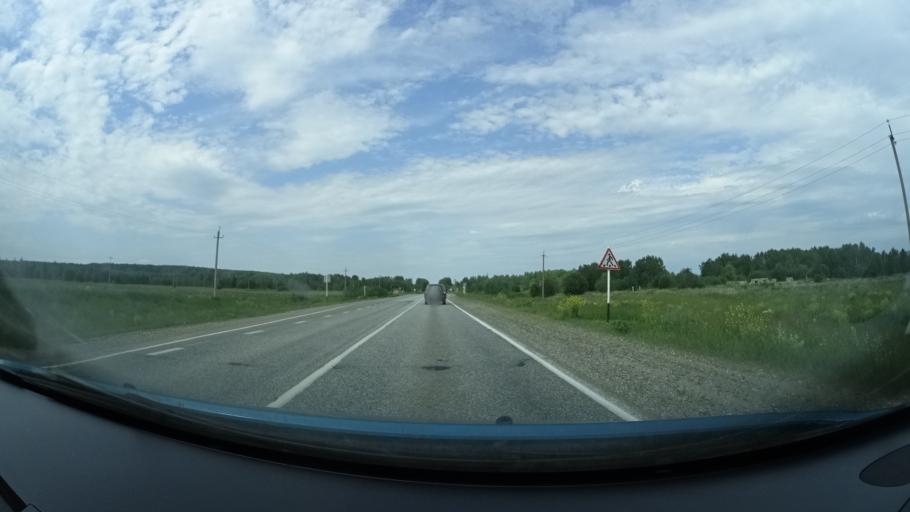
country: RU
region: Perm
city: Osa
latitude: 57.1546
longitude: 55.5297
